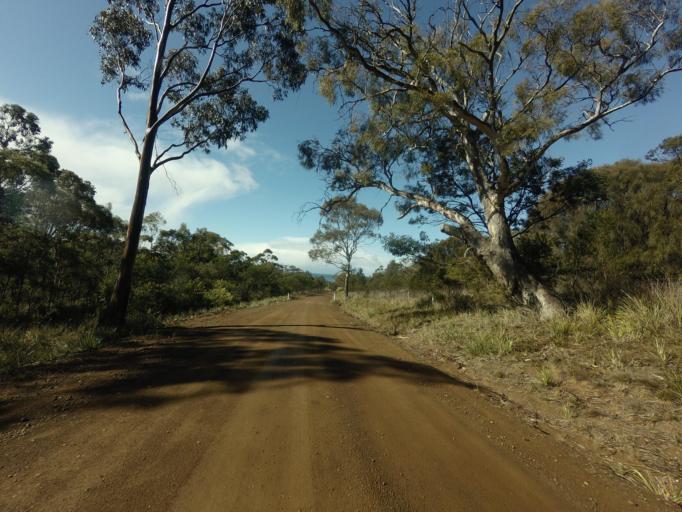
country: AU
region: Tasmania
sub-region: Sorell
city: Sorell
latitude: -42.4057
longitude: 147.9563
